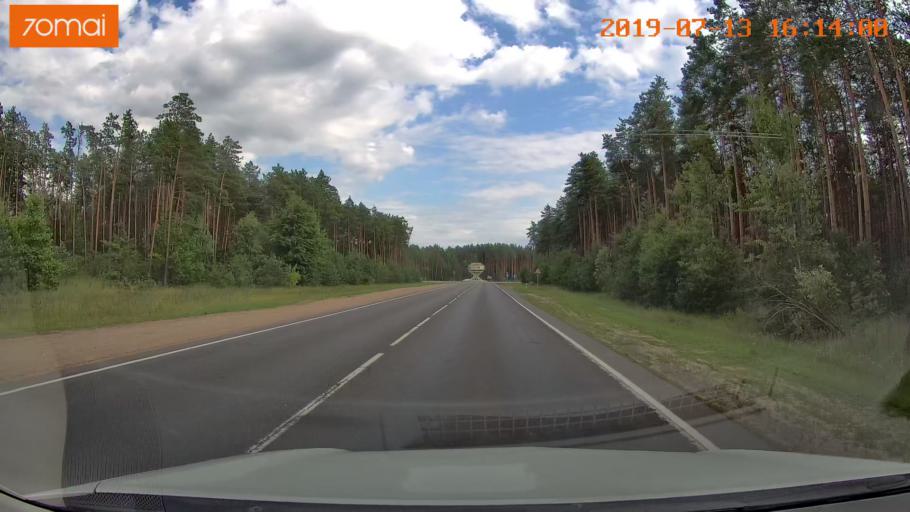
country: BY
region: Mogilev
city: Babruysk
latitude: 53.1584
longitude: 29.3143
